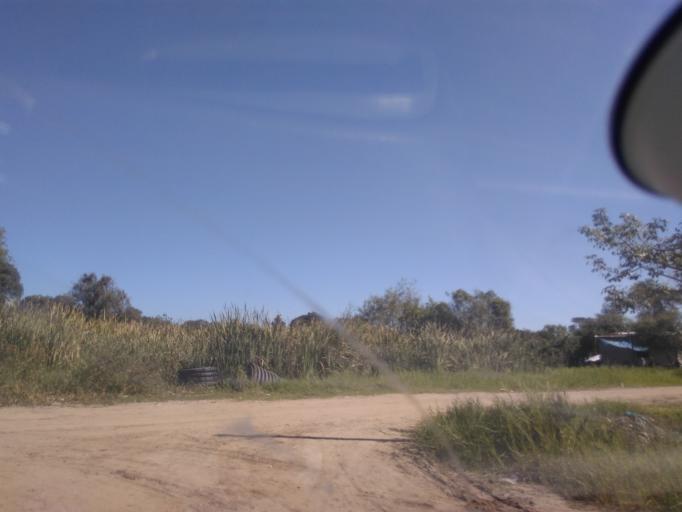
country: AR
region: Chaco
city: Fontana
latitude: -27.4301
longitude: -58.9982
